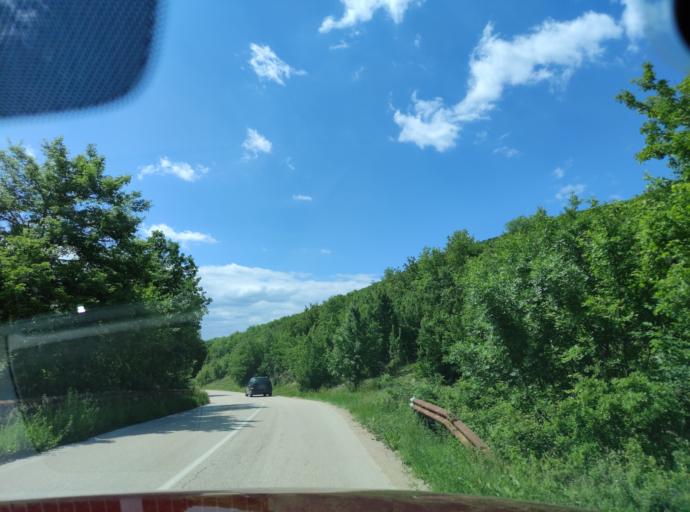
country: BG
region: Vidin
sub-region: Obshtina Ruzhintsi
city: Ruzhintsi
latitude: 43.4925
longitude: 22.8014
